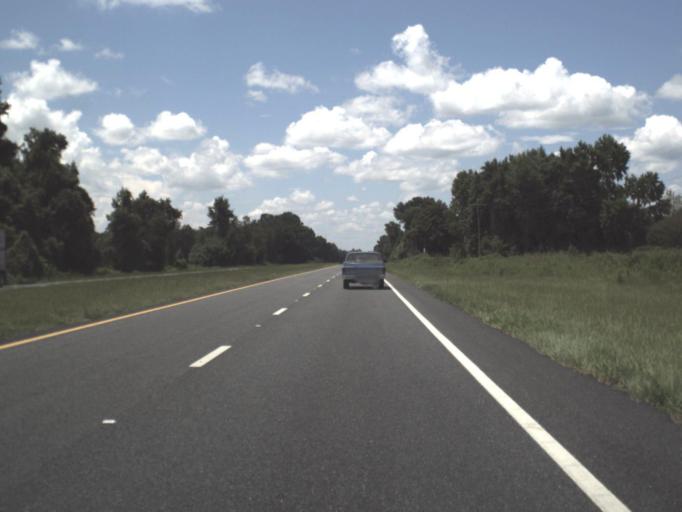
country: US
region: Florida
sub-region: Jefferson County
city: Monticello
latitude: 30.3275
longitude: -83.7711
